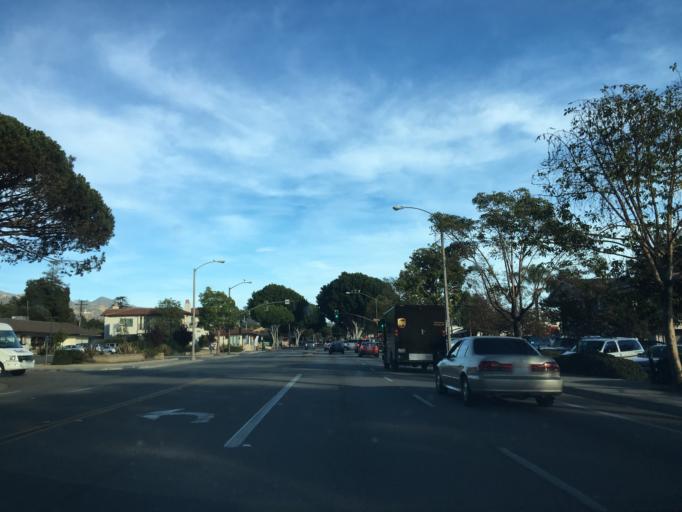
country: US
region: California
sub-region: Santa Barbara County
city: Mission Canyon
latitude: 34.4404
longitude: -119.7387
